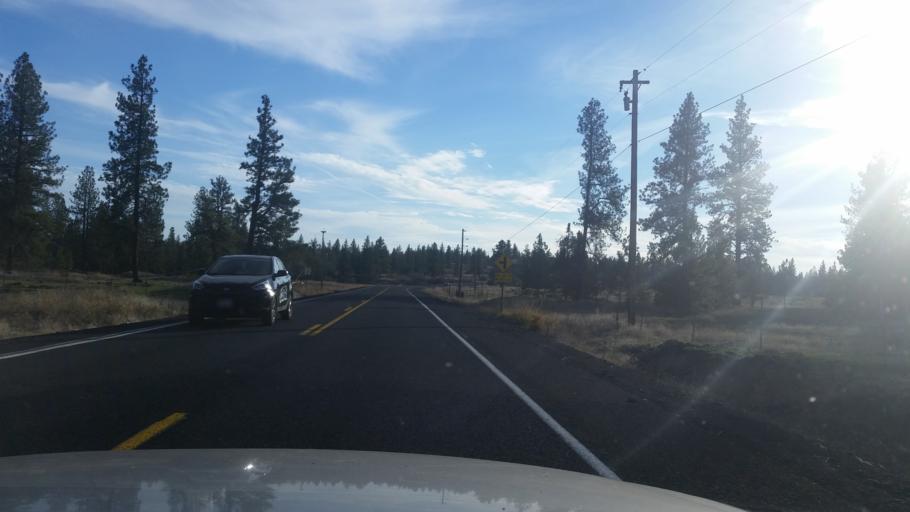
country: US
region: Washington
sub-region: Spokane County
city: Cheney
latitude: 47.3484
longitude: -117.5887
